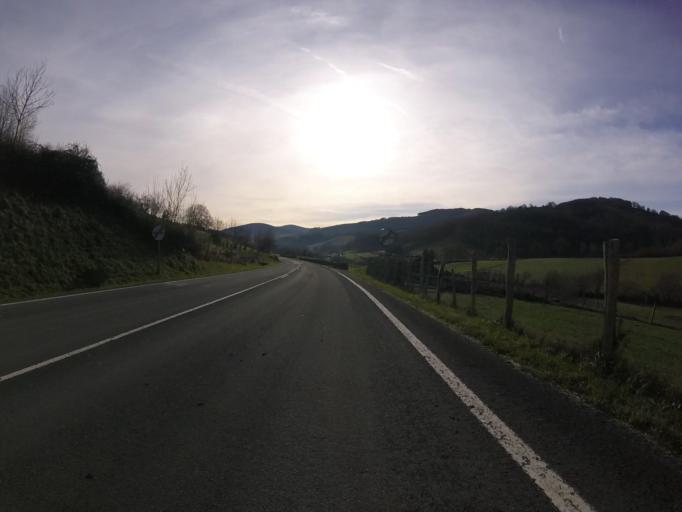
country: ES
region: Basque Country
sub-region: Provincia de Guipuzcoa
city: Berastegui
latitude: 43.1163
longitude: -1.9670
